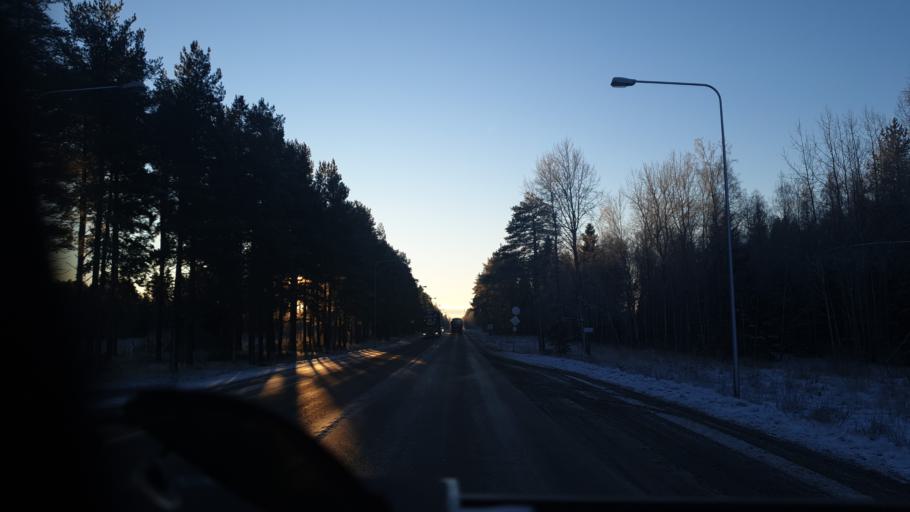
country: FI
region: Northern Ostrobothnia
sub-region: Ylivieska
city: Kalajoki
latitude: 64.2773
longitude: 23.9487
